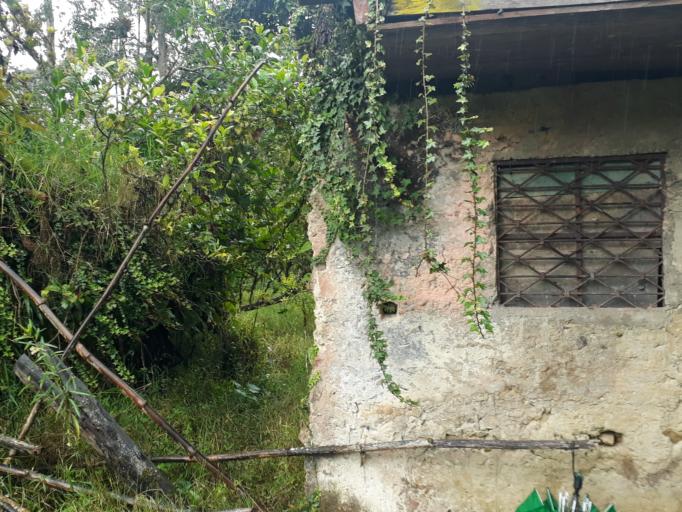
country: CO
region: Boyaca
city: Miraflores
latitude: 5.2859
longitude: -72.9788
